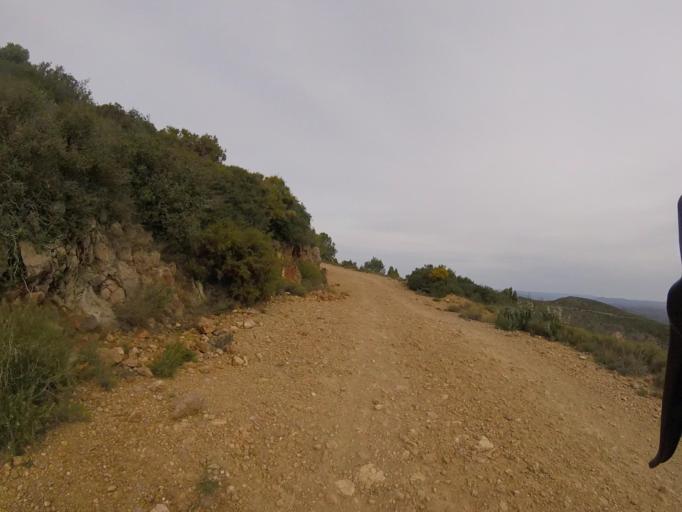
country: ES
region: Valencia
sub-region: Provincia de Castello
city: Benicassim
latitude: 40.0866
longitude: 0.0384
